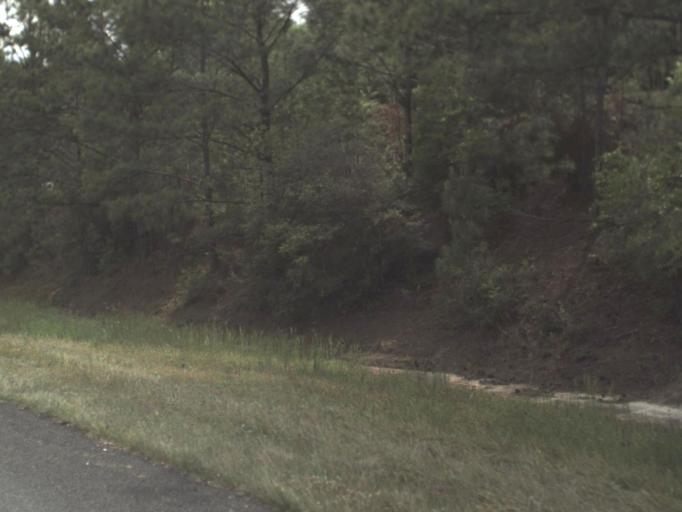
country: US
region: Florida
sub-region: Escambia County
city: Century
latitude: 30.8921
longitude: -87.3211
